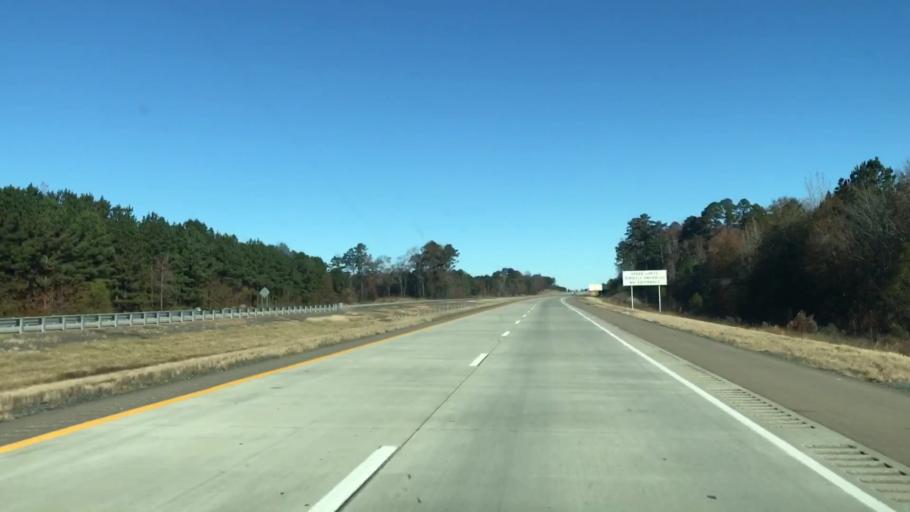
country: US
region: Louisiana
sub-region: Caddo Parish
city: Vivian
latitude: 33.0292
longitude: -93.9006
